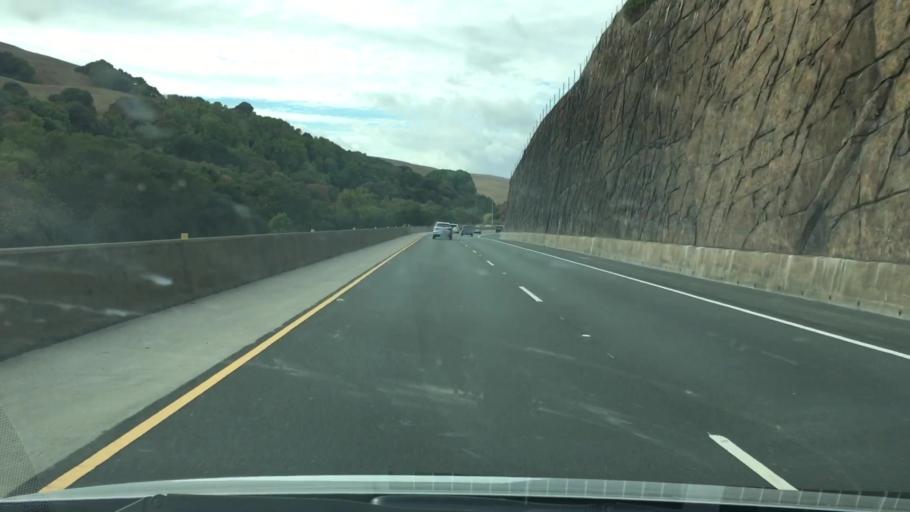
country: US
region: California
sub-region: Solano County
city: Green Valley
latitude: 38.2067
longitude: -122.1746
